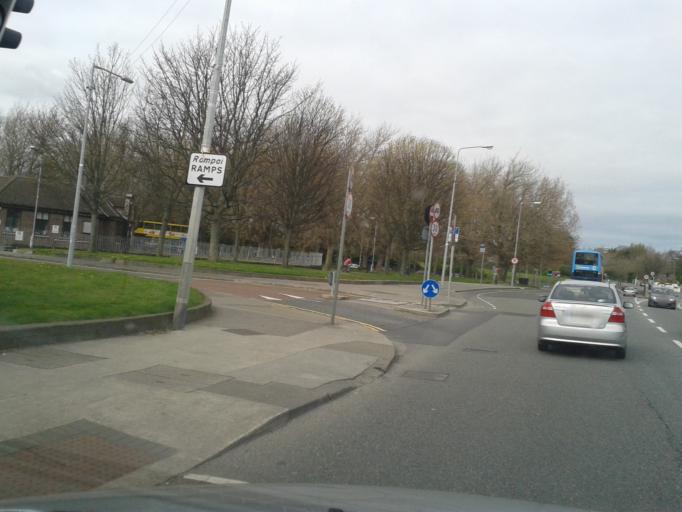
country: IE
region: Leinster
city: Marino
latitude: 53.3675
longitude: -6.2277
